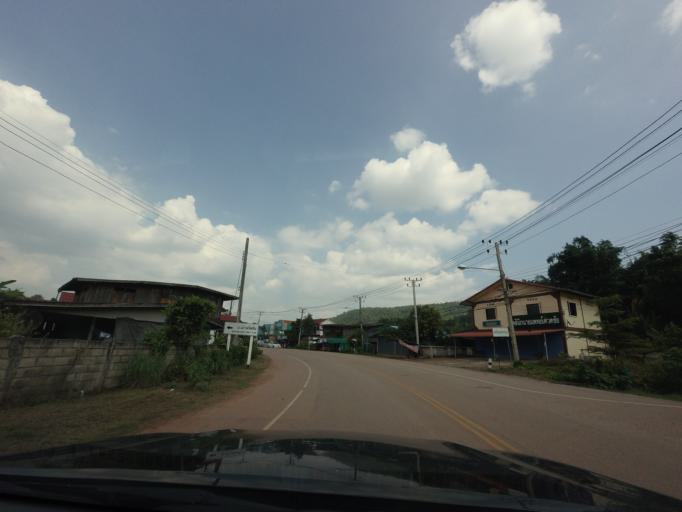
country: TH
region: Uttaradit
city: Ban Khok
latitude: 18.0204
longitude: 101.0680
